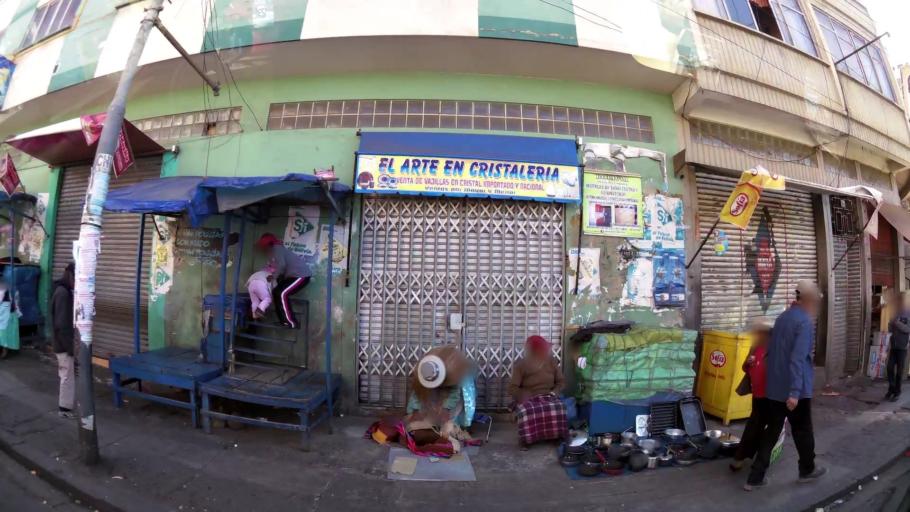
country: BO
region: La Paz
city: La Paz
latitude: -16.4975
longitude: -68.1445
